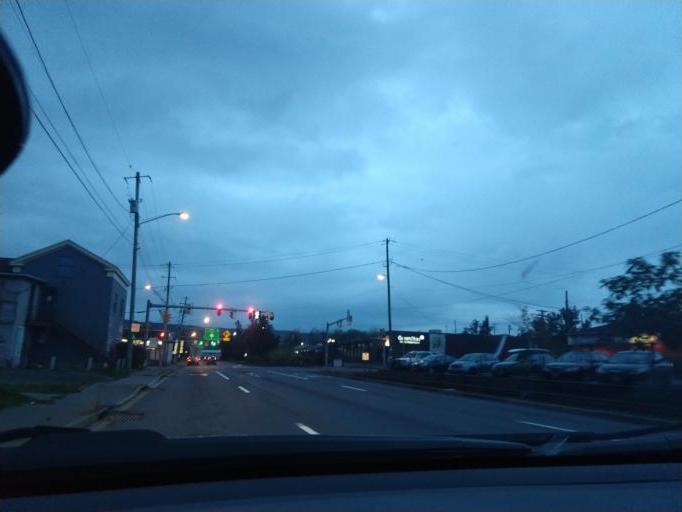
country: US
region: New York
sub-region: Tompkins County
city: Ithaca
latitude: 42.4415
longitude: -76.5106
